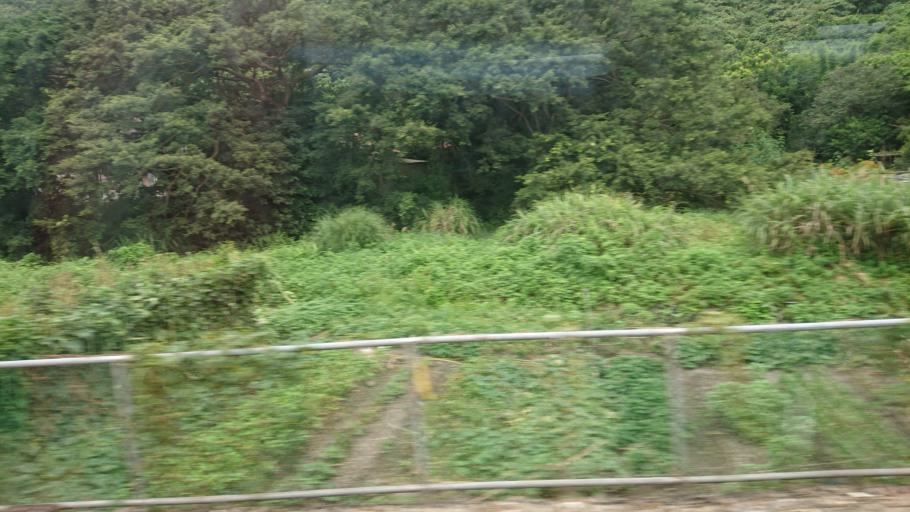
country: TW
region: Taiwan
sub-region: Yilan
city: Yilan
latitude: 24.9234
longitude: 121.8830
